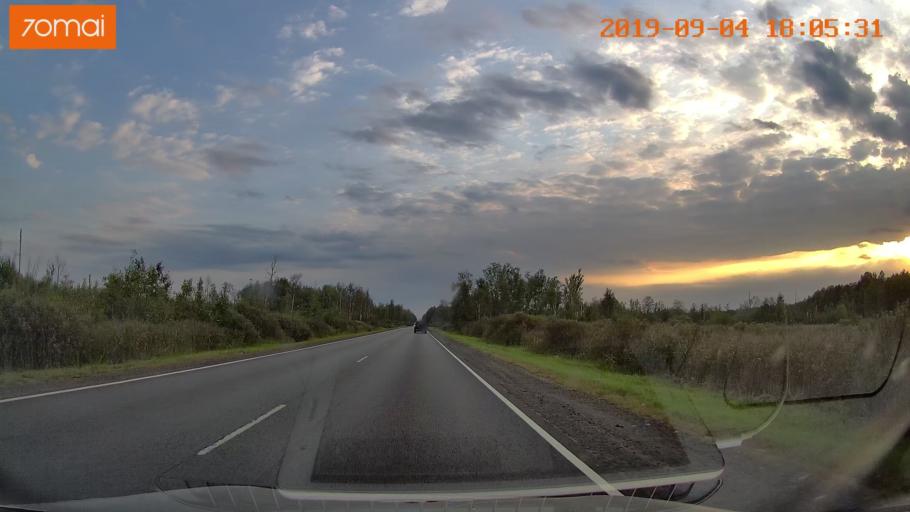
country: RU
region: Moskovskaya
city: Il'inskiy Pogost
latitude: 55.4406
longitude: 38.8257
